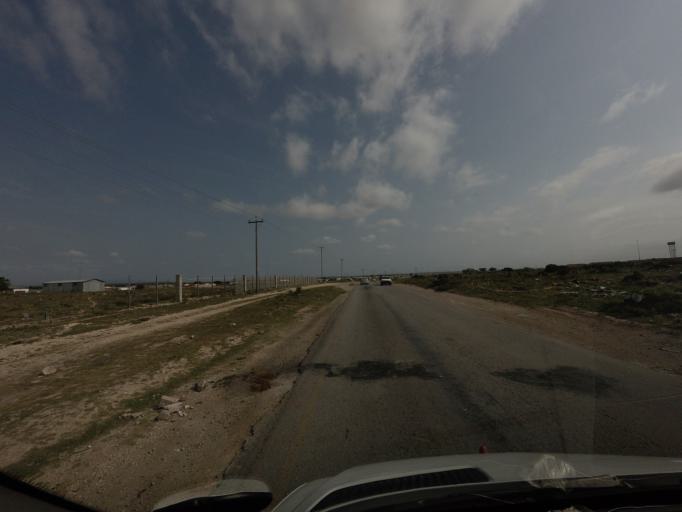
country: ZA
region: Eastern Cape
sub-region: Nelson Mandela Bay Metropolitan Municipality
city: Port Elizabeth
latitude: -33.7808
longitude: 25.5907
